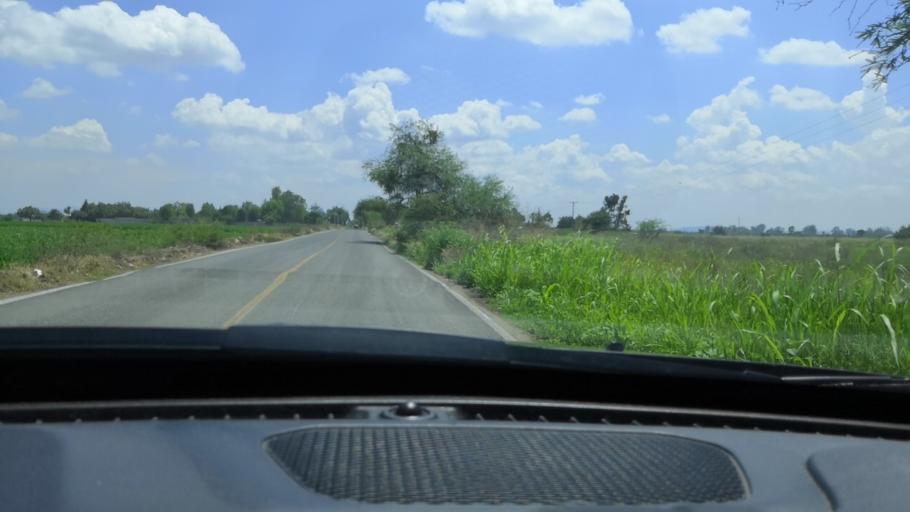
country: MX
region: Guanajuato
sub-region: Silao de la Victoria
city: El Refugio de los Sauces
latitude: 20.9530
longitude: -101.6001
